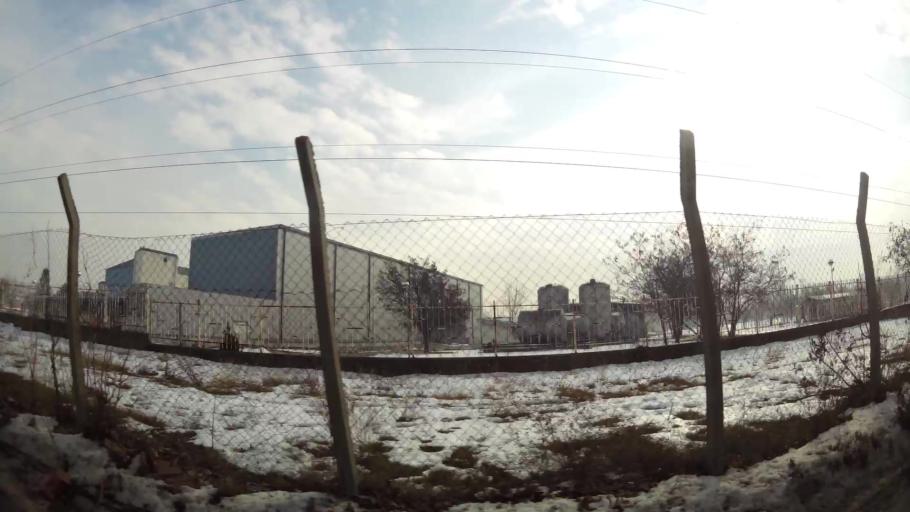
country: MK
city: Krushopek
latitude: 42.0137
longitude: 21.3628
